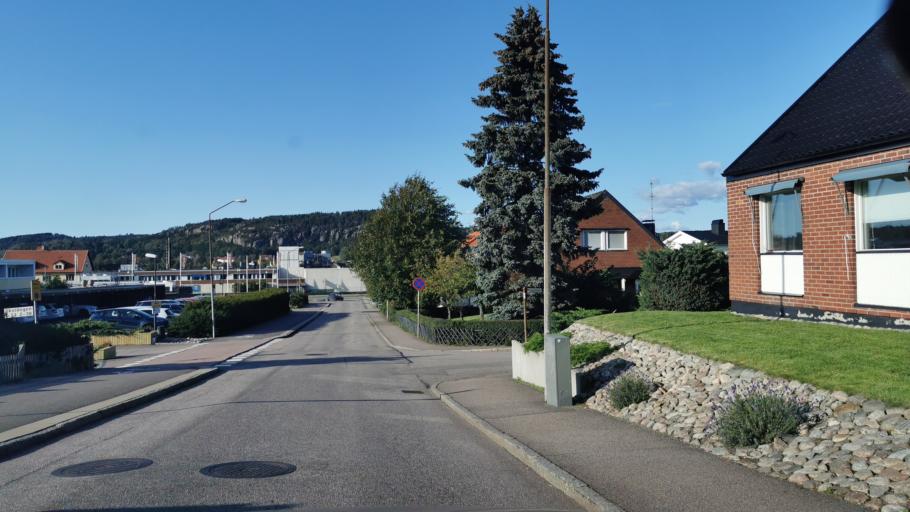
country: SE
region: Vaestra Goetaland
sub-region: Partille Kommun
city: Partille
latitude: 57.7303
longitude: 12.0703
